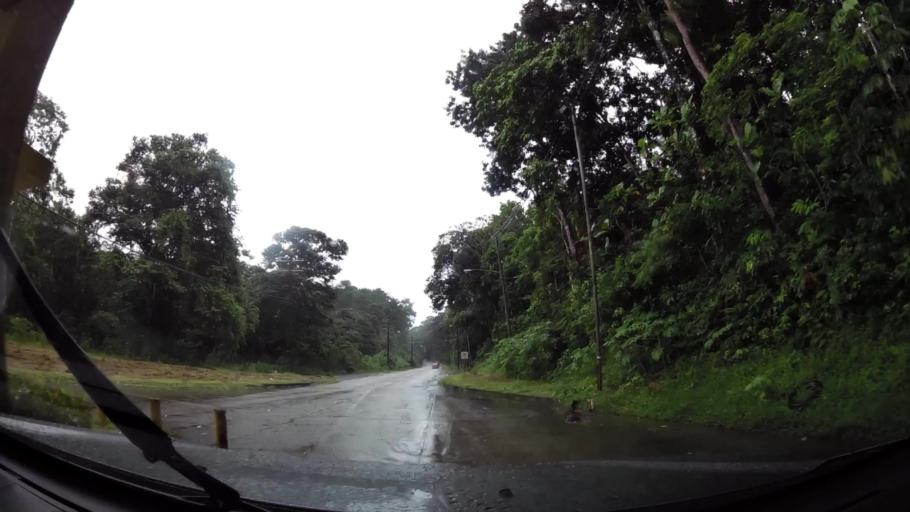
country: PA
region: Colon
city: Las Margaritas
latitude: 9.3220
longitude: -79.8846
